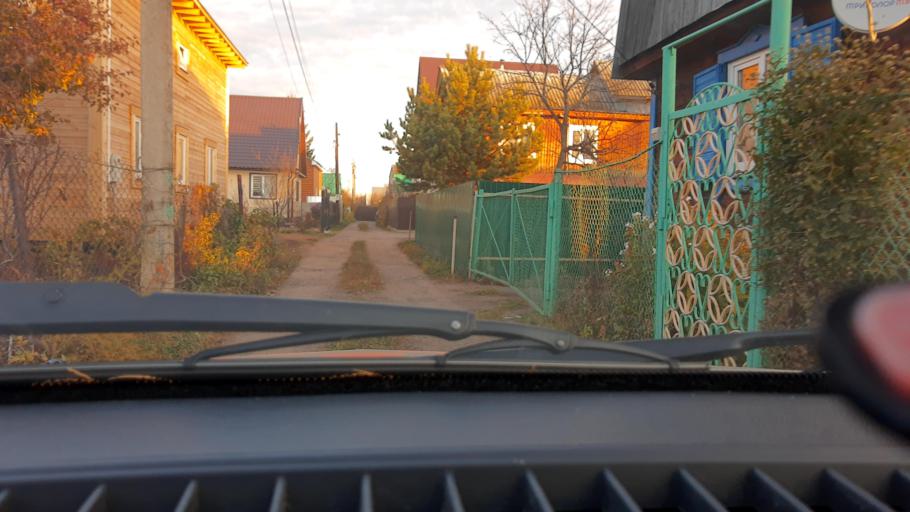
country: RU
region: Bashkortostan
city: Ufa
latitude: 54.6887
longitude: 55.9009
